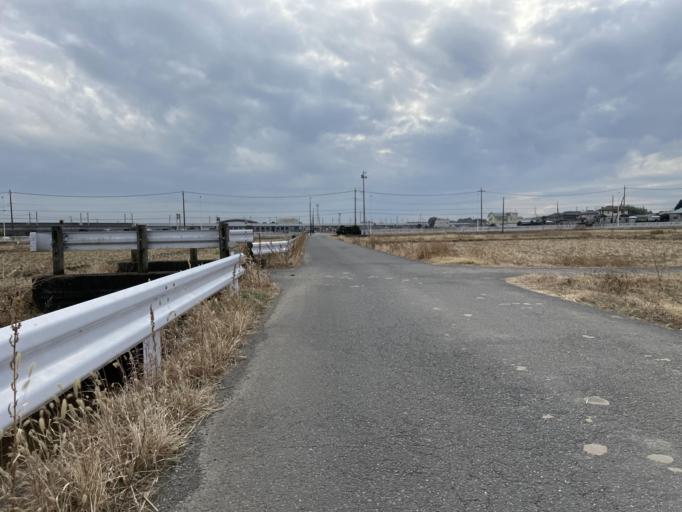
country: JP
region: Saitama
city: Shiraoka
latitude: 36.0173
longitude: 139.6467
